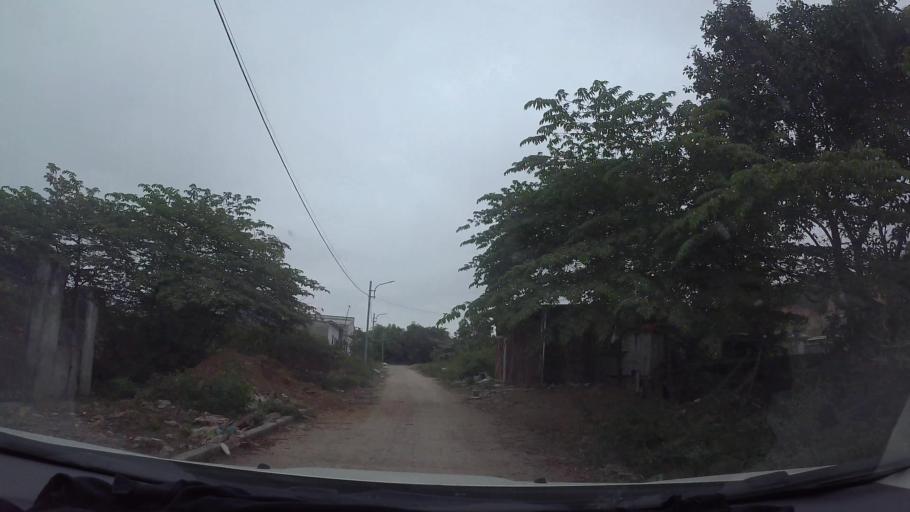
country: VN
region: Da Nang
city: Lien Chieu
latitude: 16.0700
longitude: 108.1387
